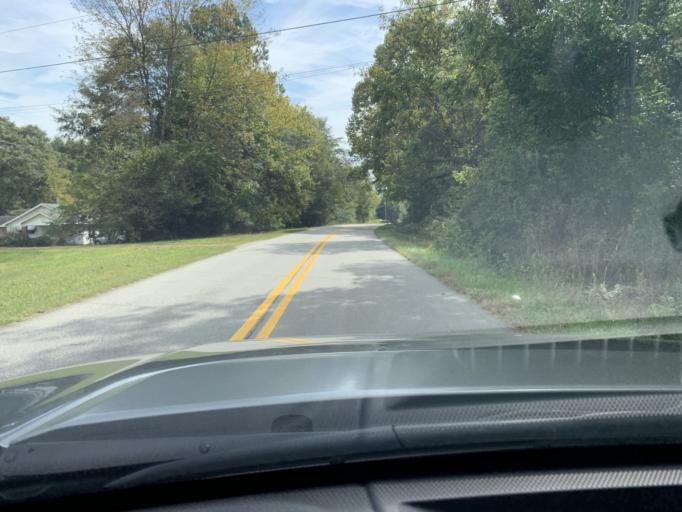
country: US
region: Georgia
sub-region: Polk County
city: Cedartown
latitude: 33.9732
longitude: -85.2714
